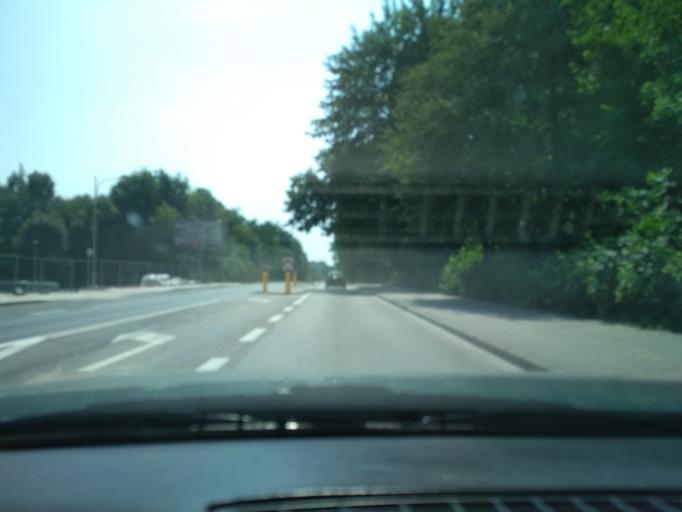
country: PL
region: Silesian Voivodeship
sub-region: Chorzow
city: Chorzow
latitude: 50.2942
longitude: 19.0047
